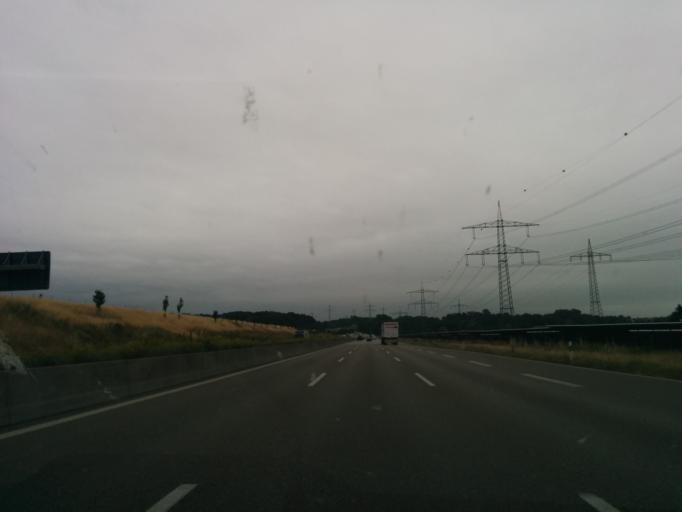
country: DE
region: Bavaria
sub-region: Swabia
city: Friedberg
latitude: 48.4040
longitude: 10.9551
